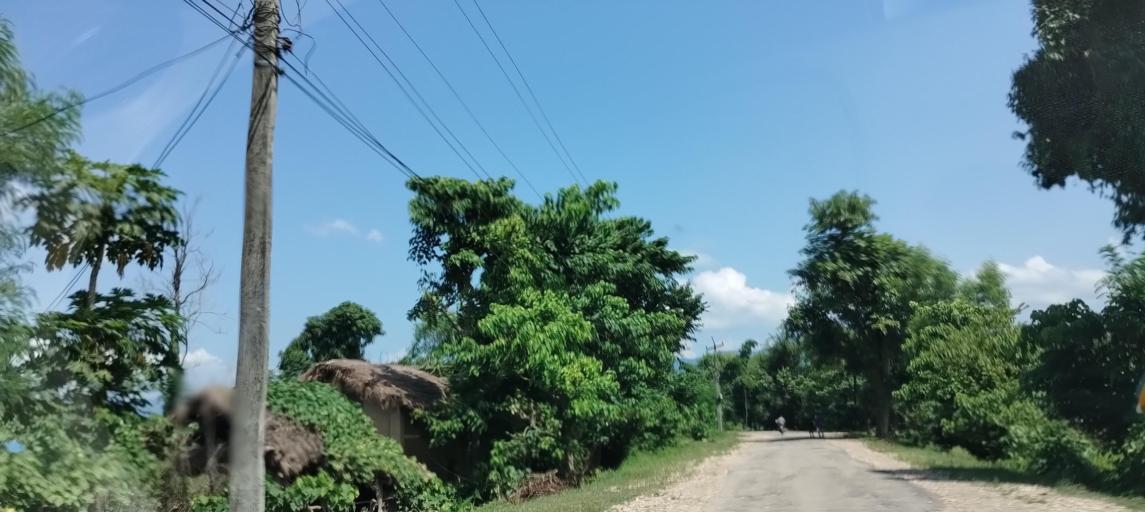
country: NP
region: Far Western
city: Tikapur
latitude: 28.5043
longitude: 81.3024
